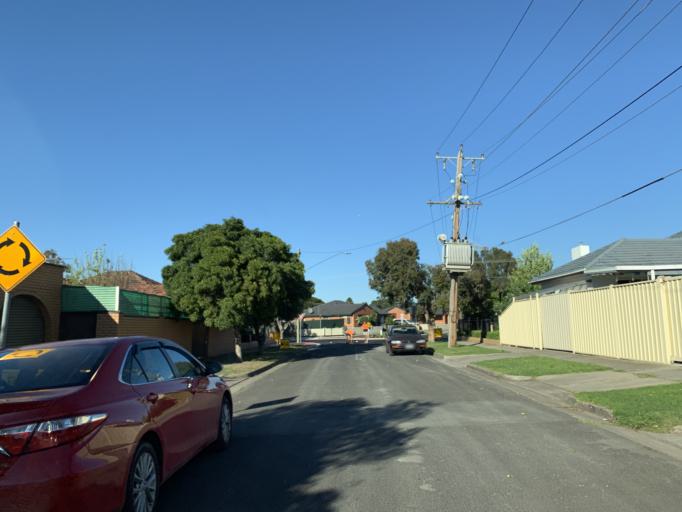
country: AU
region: Victoria
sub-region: Brimbank
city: St Albans
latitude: -37.7540
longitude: 144.8047
